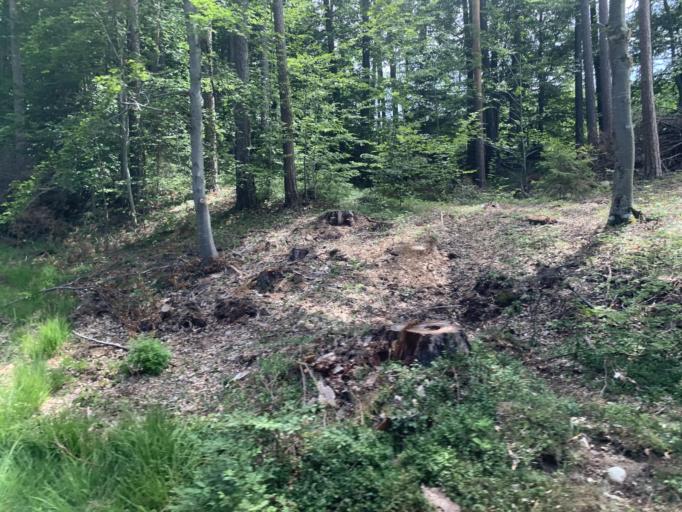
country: IT
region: Trentino-Alto Adige
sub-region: Bolzano
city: Soprabolzano
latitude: 46.5266
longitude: 11.4322
